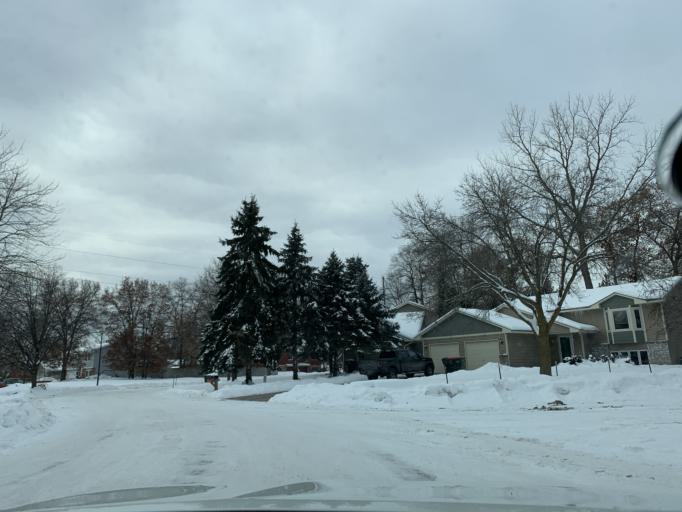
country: US
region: Minnesota
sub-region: Hennepin County
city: West Coon Rapids
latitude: 45.1687
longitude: -93.3015
